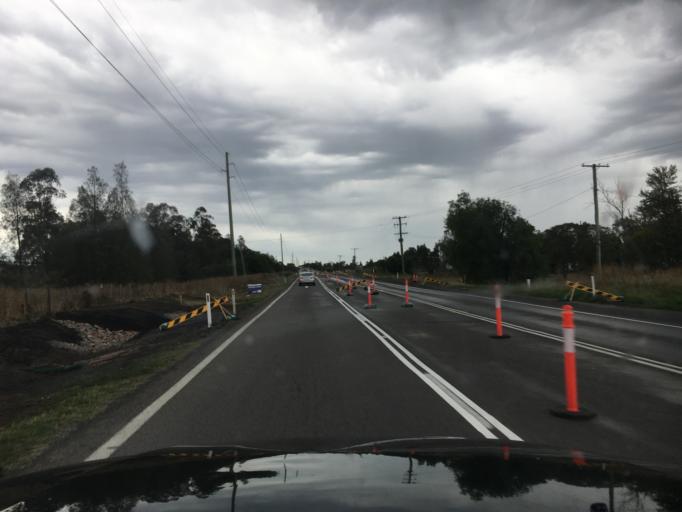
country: AU
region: New South Wales
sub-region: Muswellbrook
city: Muswellbrook
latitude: -32.1917
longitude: 150.8928
